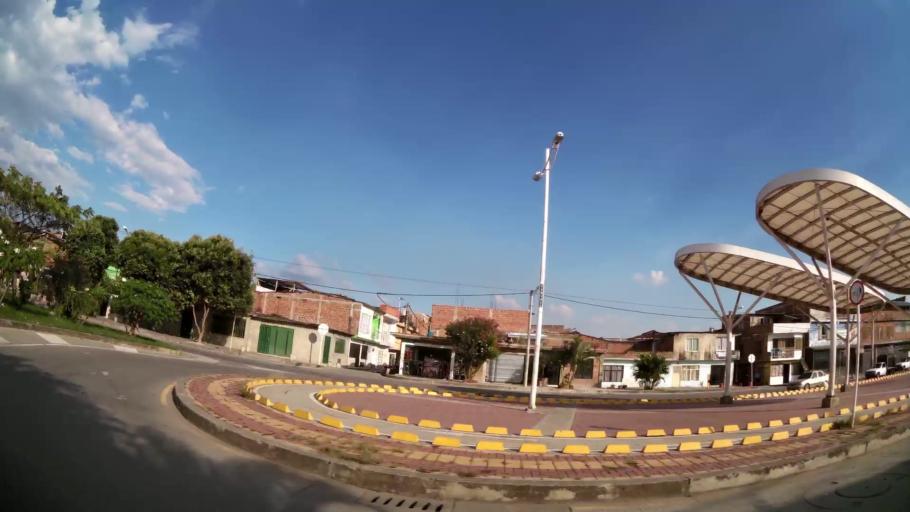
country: CO
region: Valle del Cauca
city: Cali
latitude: 3.4234
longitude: -76.4889
